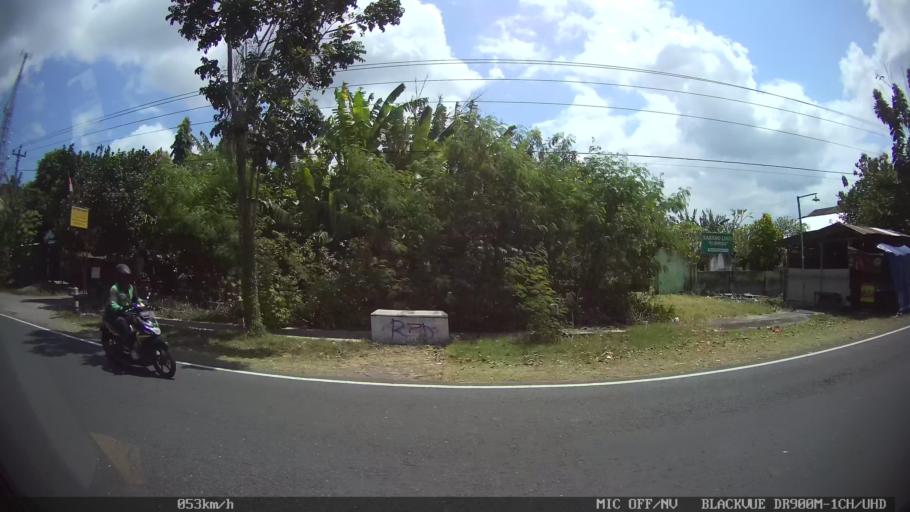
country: ID
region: Daerah Istimewa Yogyakarta
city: Sewon
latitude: -7.8841
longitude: 110.3471
